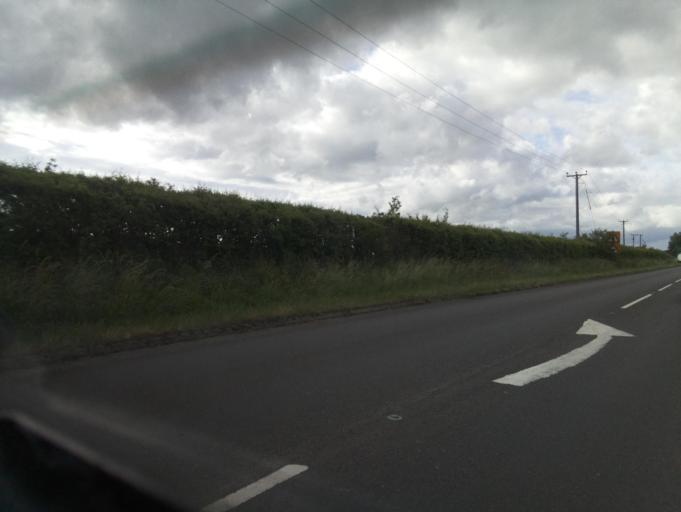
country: GB
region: England
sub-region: Worcestershire
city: Kidderminster
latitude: 52.4381
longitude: -2.2119
